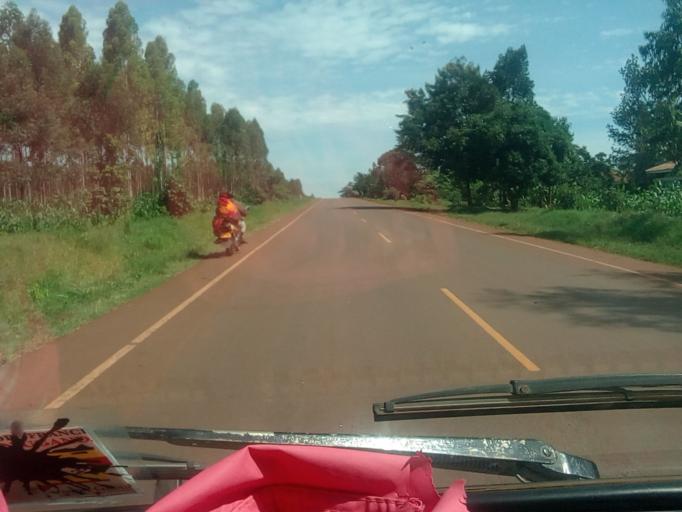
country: UG
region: Eastern Region
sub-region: Luuka District
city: Luuka Town
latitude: 0.6401
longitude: 33.2718
